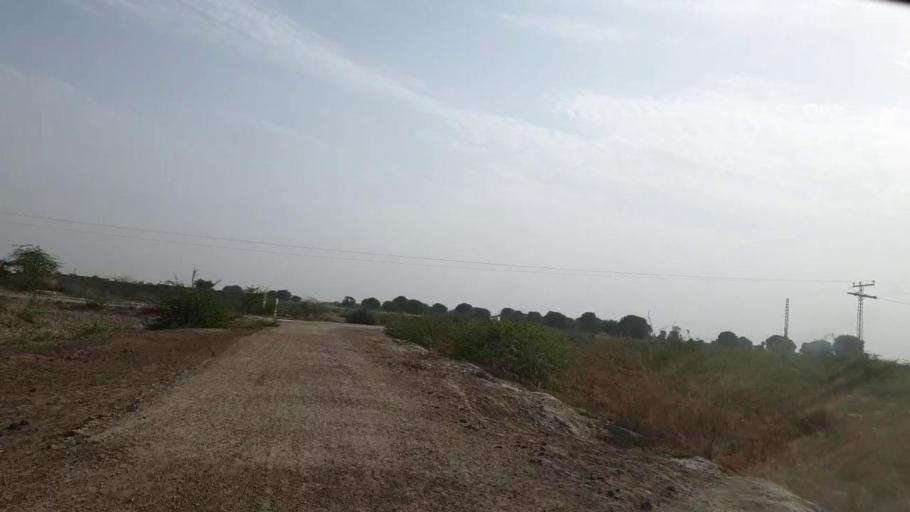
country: PK
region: Sindh
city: Nabisar
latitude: 24.9837
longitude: 69.5076
